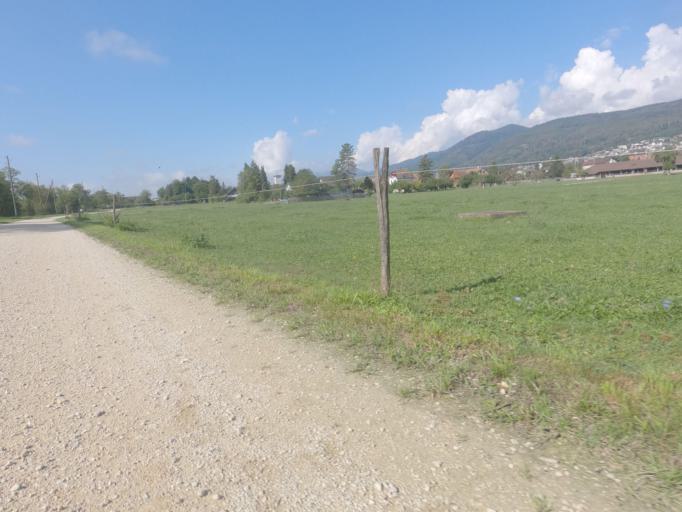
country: CH
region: Solothurn
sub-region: Bezirk Olten
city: Hagendorf
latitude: 47.3300
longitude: 7.8515
